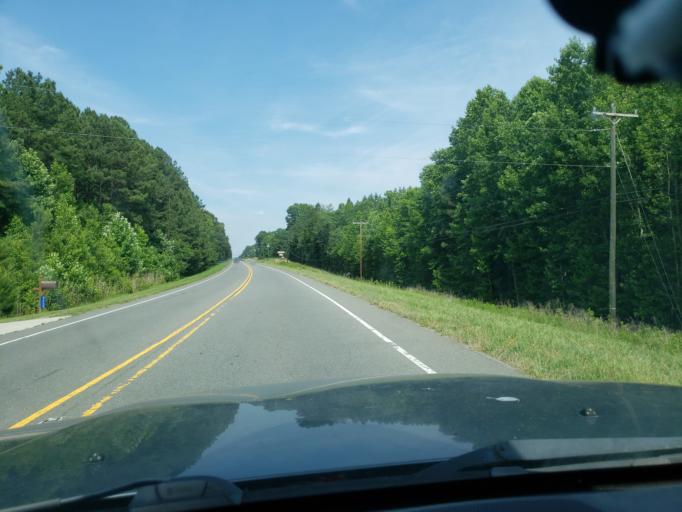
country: US
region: North Carolina
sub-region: Orange County
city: Carrboro
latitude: 35.9221
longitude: -79.1849
